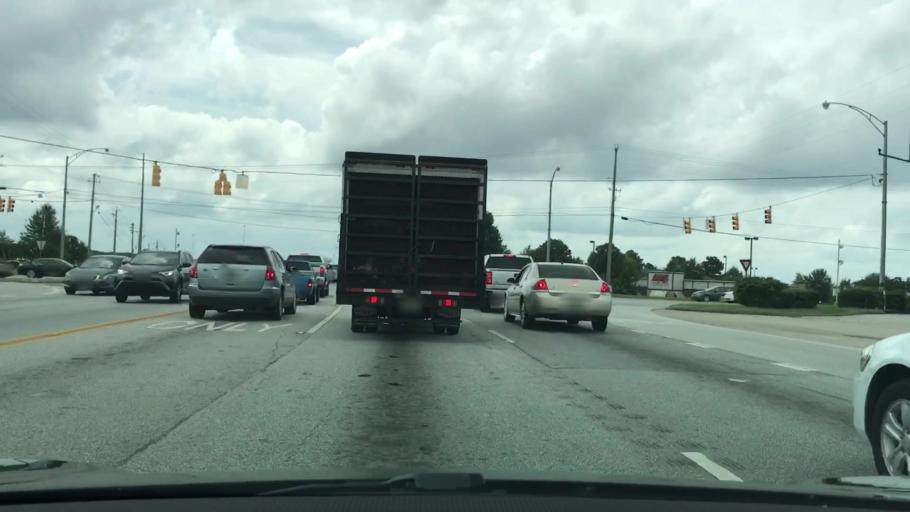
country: US
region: Alabama
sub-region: Lee County
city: Opelika
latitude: 32.6232
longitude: -85.4051
